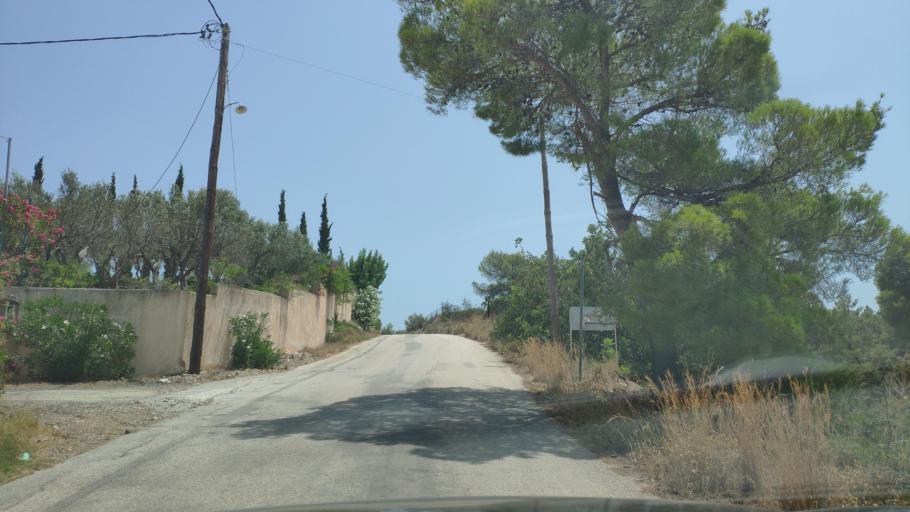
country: GR
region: Peloponnese
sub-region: Nomos Argolidos
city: Porto Cheli
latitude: 37.3087
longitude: 23.1504
